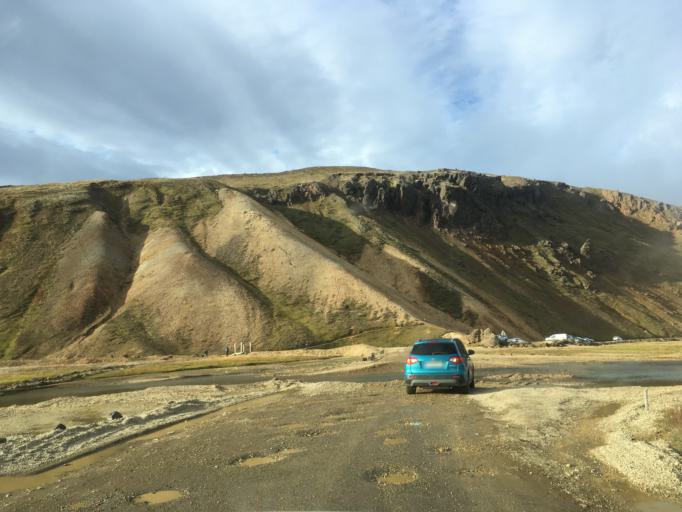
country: IS
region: South
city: Vestmannaeyjar
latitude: 63.9934
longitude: -19.0600
